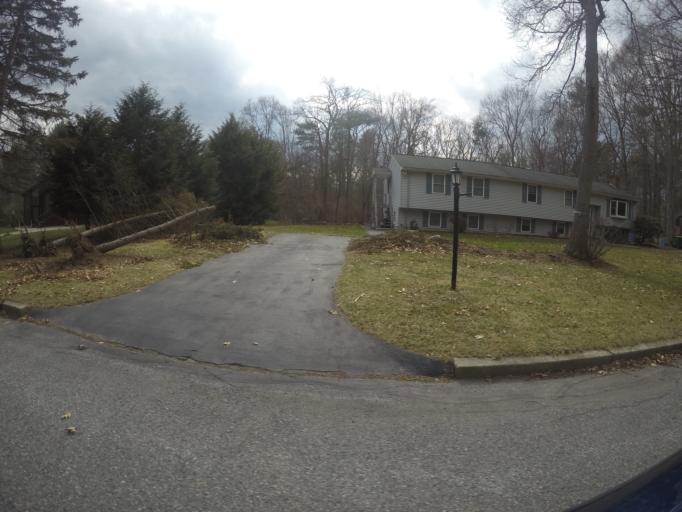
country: US
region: Massachusetts
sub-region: Bristol County
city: Easton
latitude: 42.0361
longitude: -71.1137
